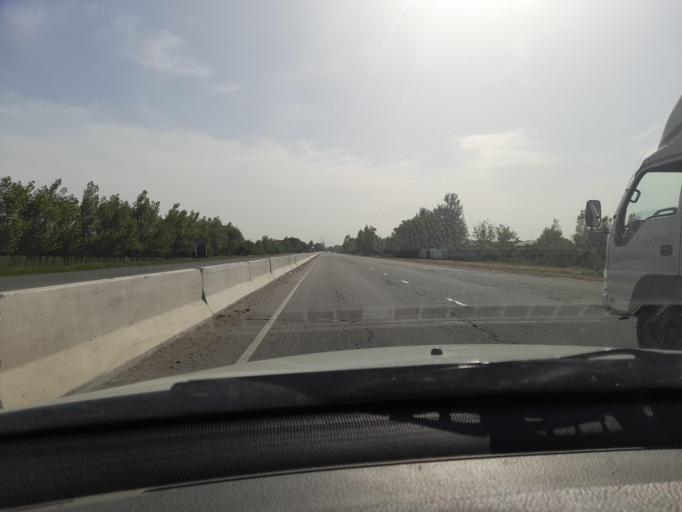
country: UZ
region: Samarqand
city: Ishtixon
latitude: 39.9423
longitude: 66.3980
